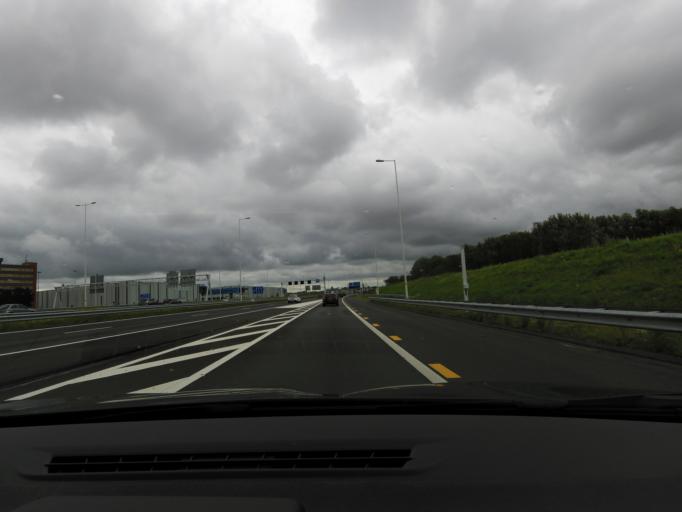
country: NL
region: South Holland
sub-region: Gemeente Albrandswaard
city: Rhoon
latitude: 51.8733
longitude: 4.4026
